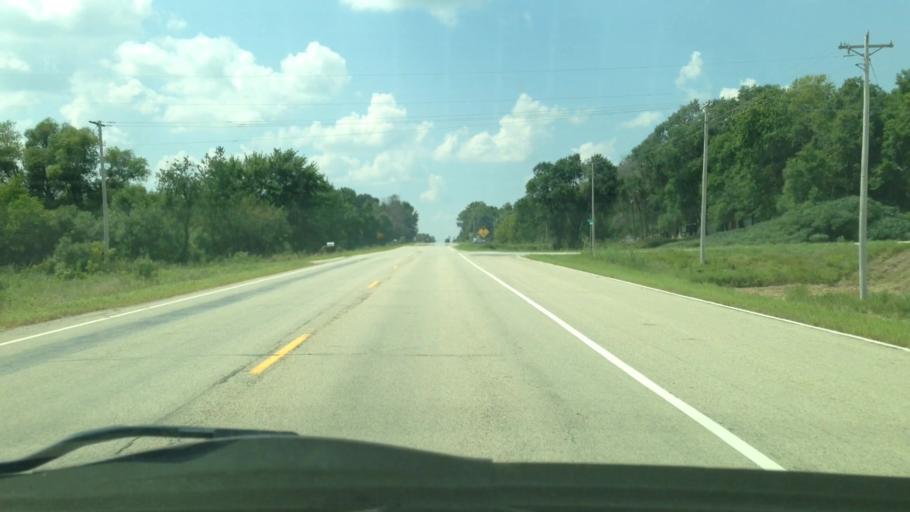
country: US
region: Minnesota
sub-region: Olmsted County
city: Stewartville
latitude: 43.8556
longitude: -92.4674
